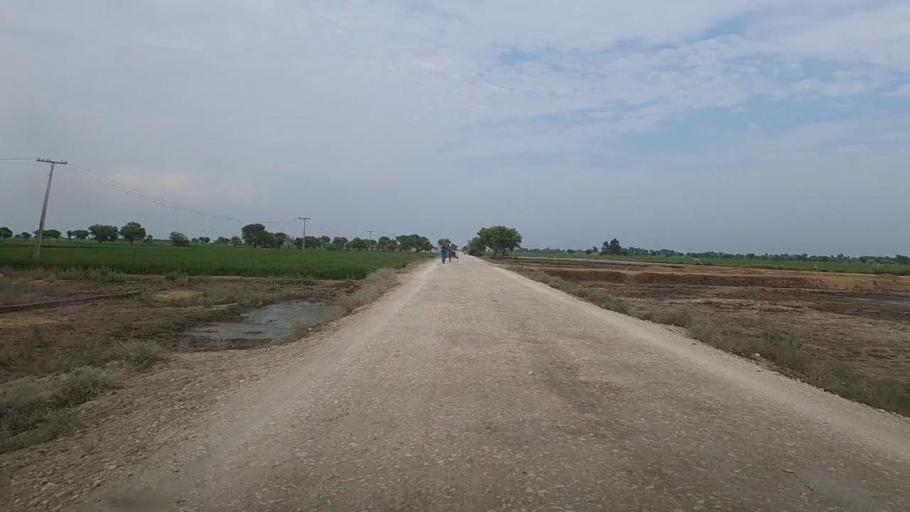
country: PK
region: Sindh
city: Thul
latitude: 28.2468
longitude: 68.7894
